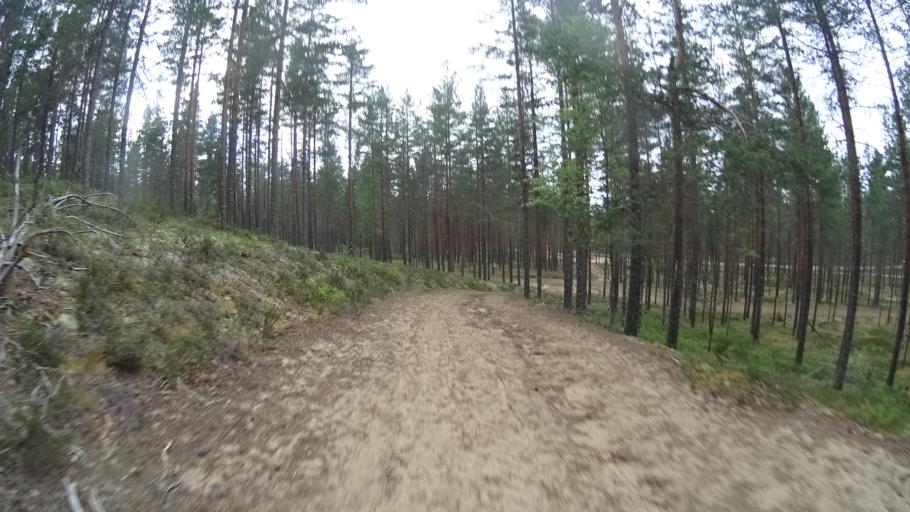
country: FI
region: Satakunta
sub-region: Pohjois-Satakunta
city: Jaemijaervi
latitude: 61.7743
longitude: 22.7313
